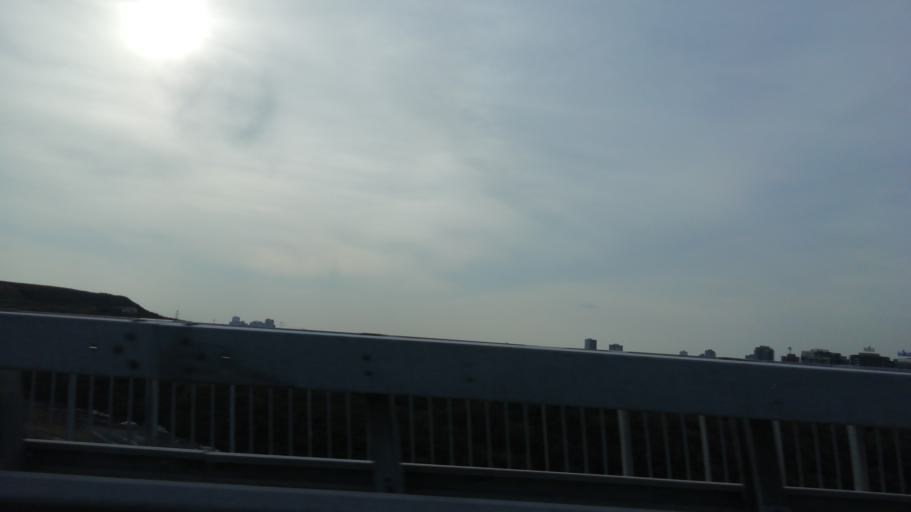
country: TR
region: Istanbul
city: Basaksehir
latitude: 41.1244
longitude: 28.7978
